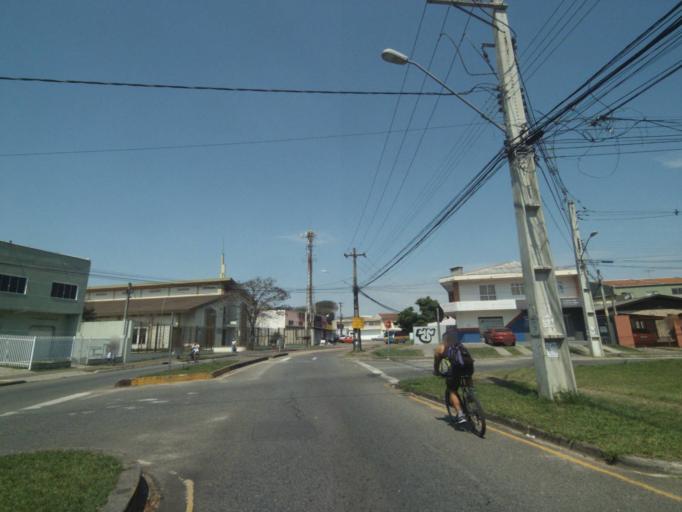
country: BR
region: Parana
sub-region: Curitiba
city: Curitiba
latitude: -25.4801
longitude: -49.3235
